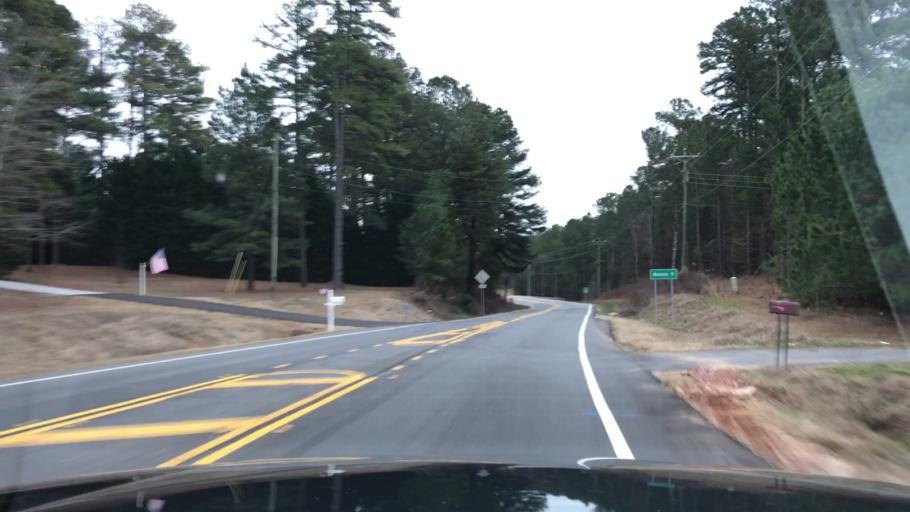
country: US
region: Georgia
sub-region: Barrow County
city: Auburn
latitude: 33.9004
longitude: -83.7997
